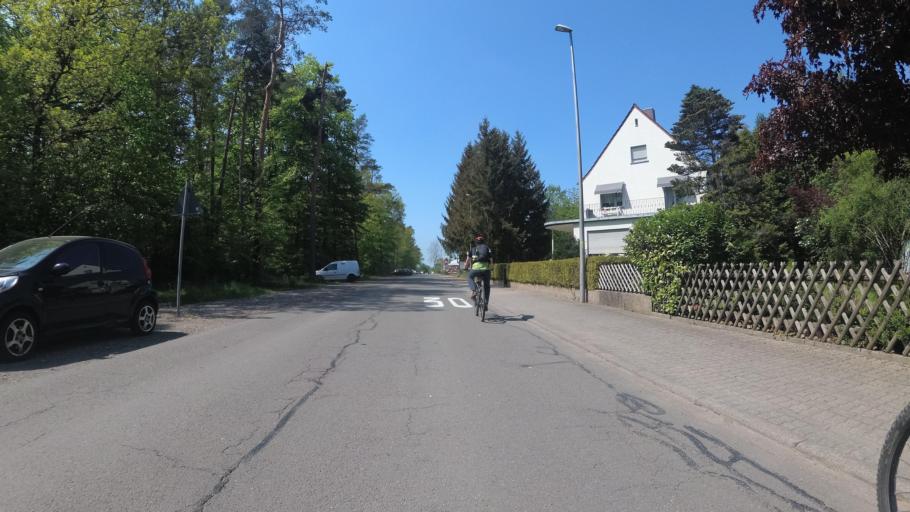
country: DE
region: Rheinland-Pfalz
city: Ramstein-Miesenbach
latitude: 49.4427
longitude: 7.5692
